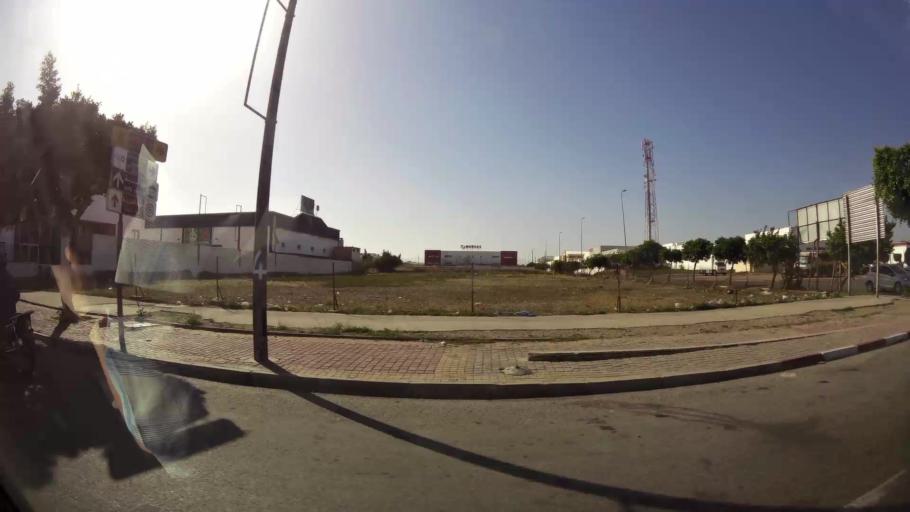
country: MA
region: Souss-Massa-Draa
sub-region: Inezgane-Ait Mellou
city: Inezgane
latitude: 30.3884
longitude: -9.5138
